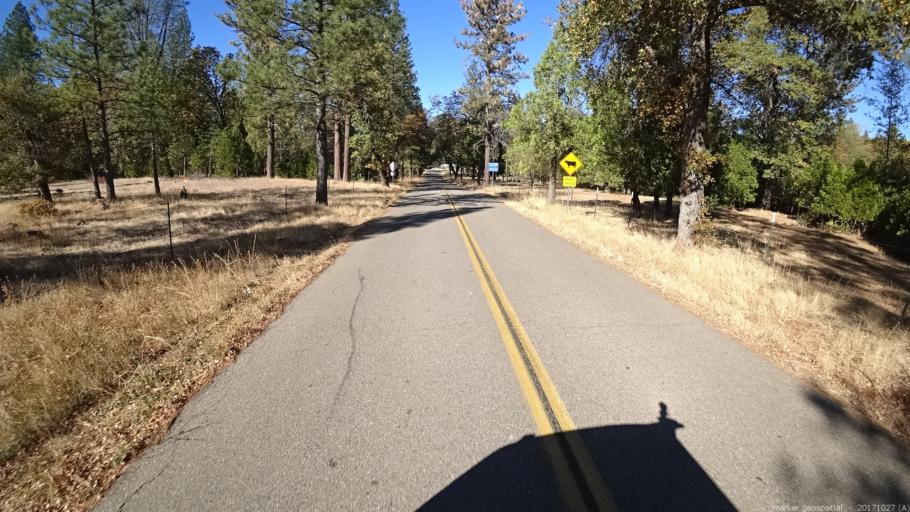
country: US
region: California
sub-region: Shasta County
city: Shingletown
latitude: 40.6325
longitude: -121.8870
